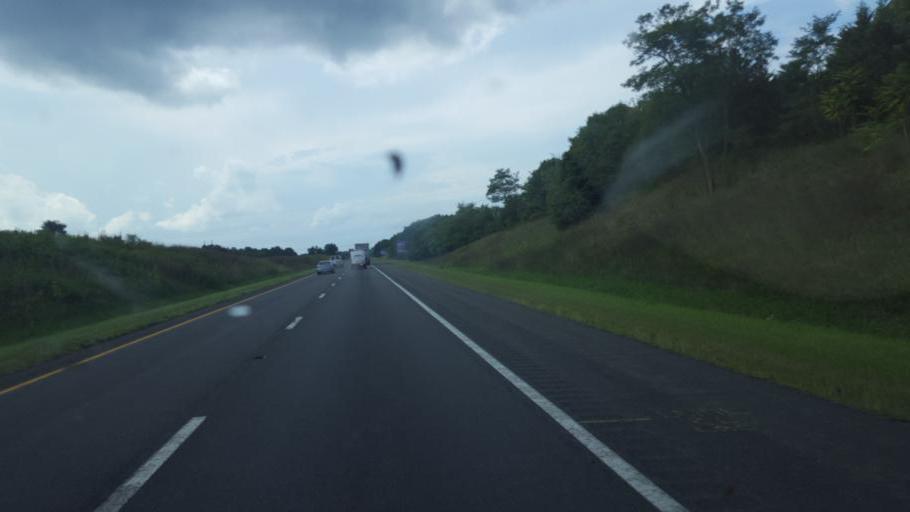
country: US
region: Virginia
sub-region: Warren County
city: Front Royal
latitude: 38.9500
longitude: -78.1665
